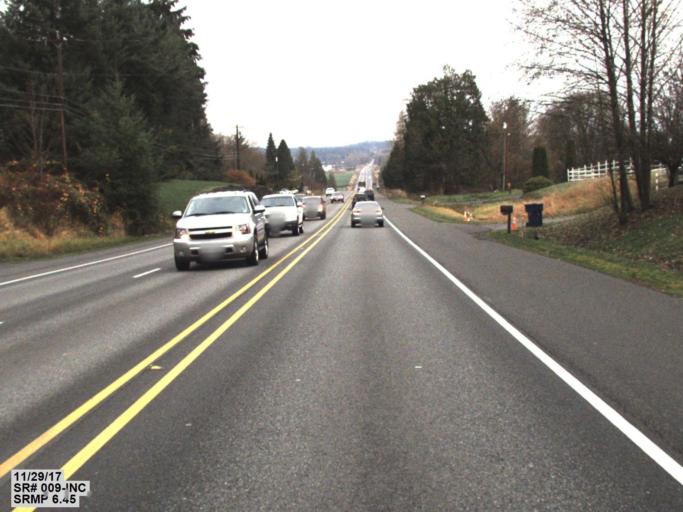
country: US
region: Washington
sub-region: Snohomish County
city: Cathcart
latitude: 47.8704
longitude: -122.1098
